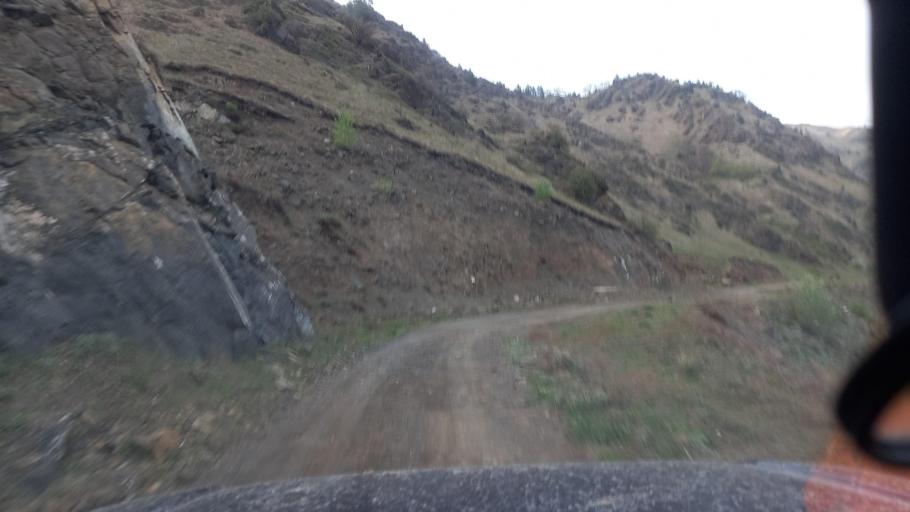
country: RU
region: Kabardino-Balkariya
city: Kamennomostskoye
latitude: 43.7217
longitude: 42.8453
